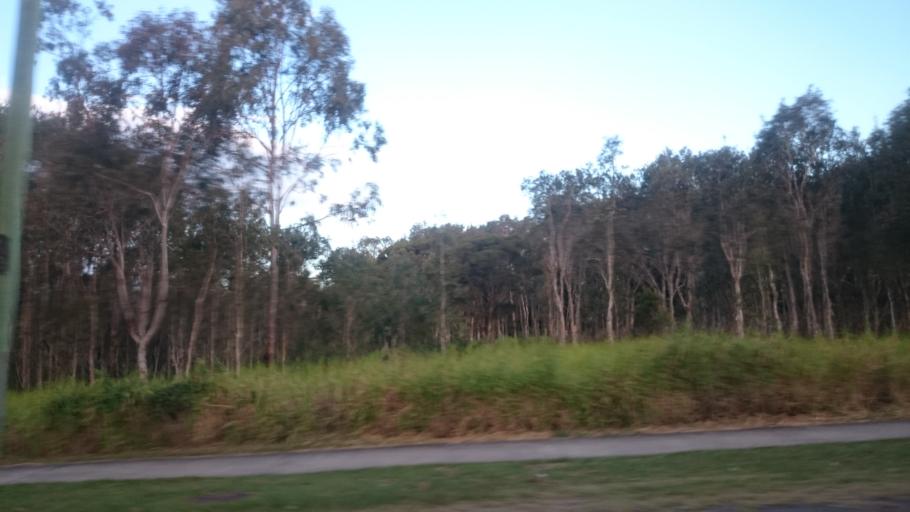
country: AU
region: Queensland
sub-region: Brisbane
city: Wynnum West
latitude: -27.4638
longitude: 153.1444
